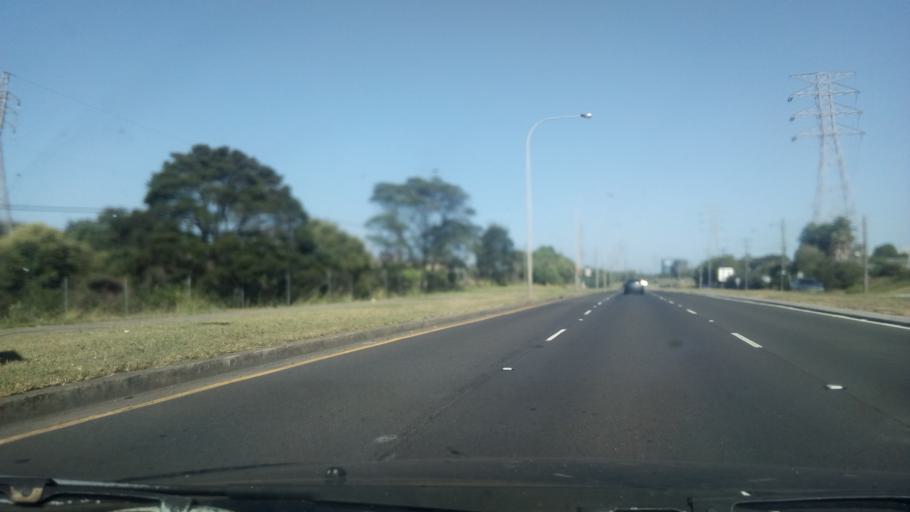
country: AU
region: New South Wales
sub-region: Wollongong
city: Mount Saint Thomas
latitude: -34.4566
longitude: 150.8604
